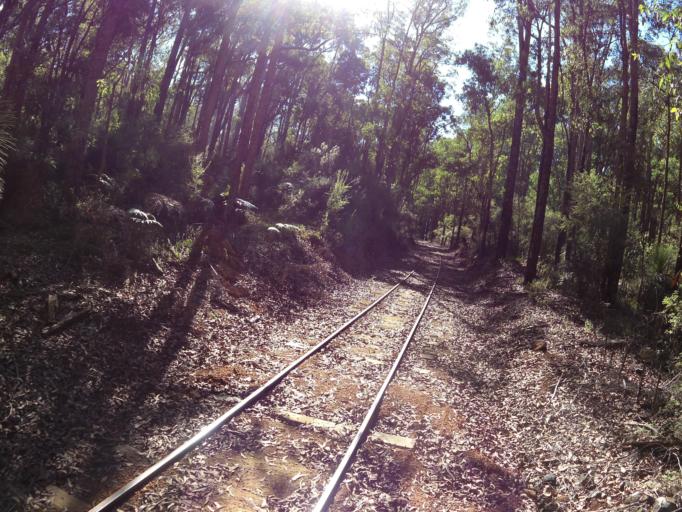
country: AU
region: Western Australia
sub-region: Waroona
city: Waroona
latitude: -32.7245
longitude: 116.1093
